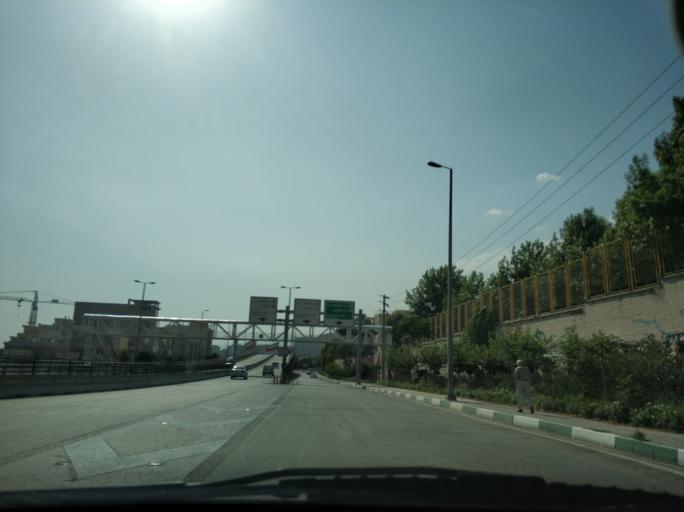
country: IR
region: Tehran
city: Tajrish
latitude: 35.7586
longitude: 51.5394
